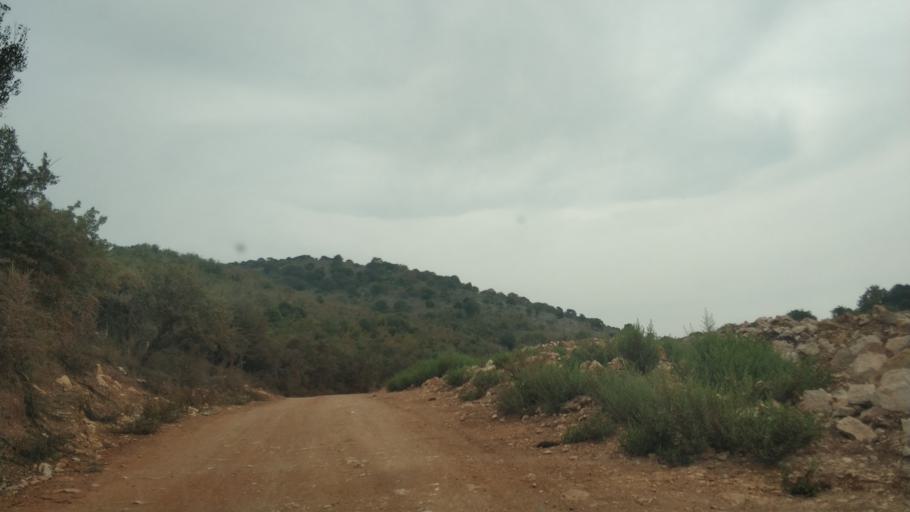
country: AL
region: Vlore
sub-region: Rrethi i Sarandes
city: Sarande
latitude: 39.7986
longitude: 20.0009
